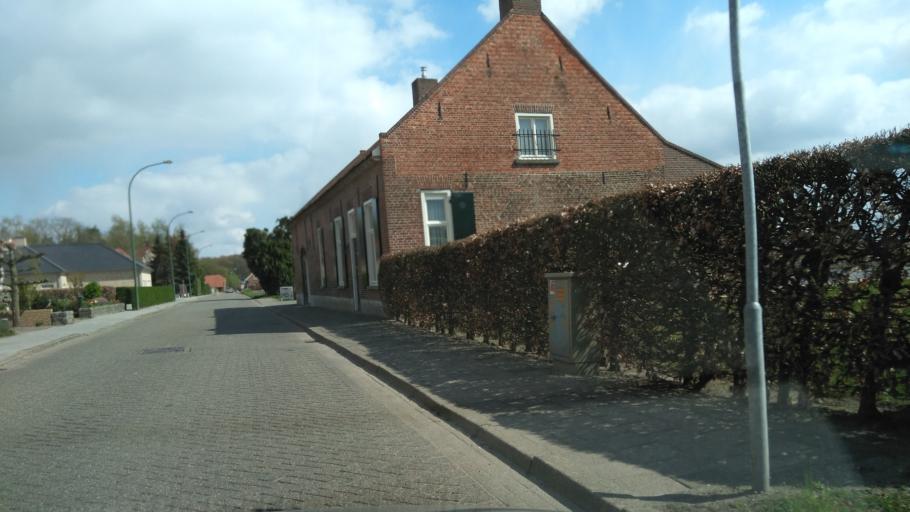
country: NL
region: North Brabant
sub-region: Gemeente Baarle-Nassau
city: Baarle-Nassau
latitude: 51.4419
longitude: 4.9376
